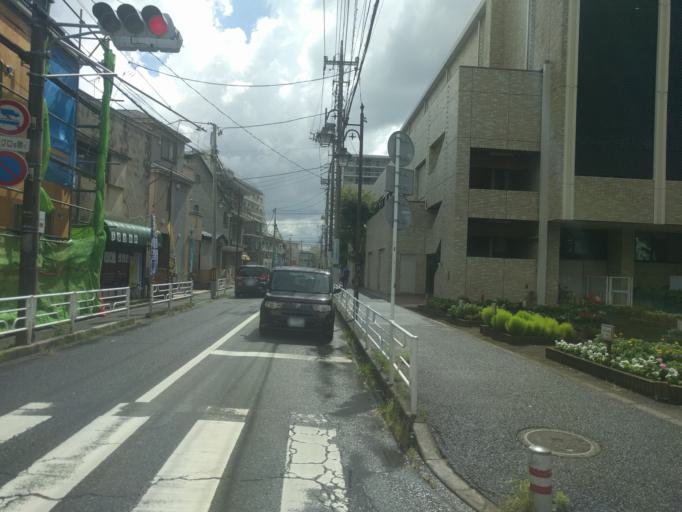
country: JP
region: Saitama
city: Shimotoda
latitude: 35.8310
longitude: 139.6812
